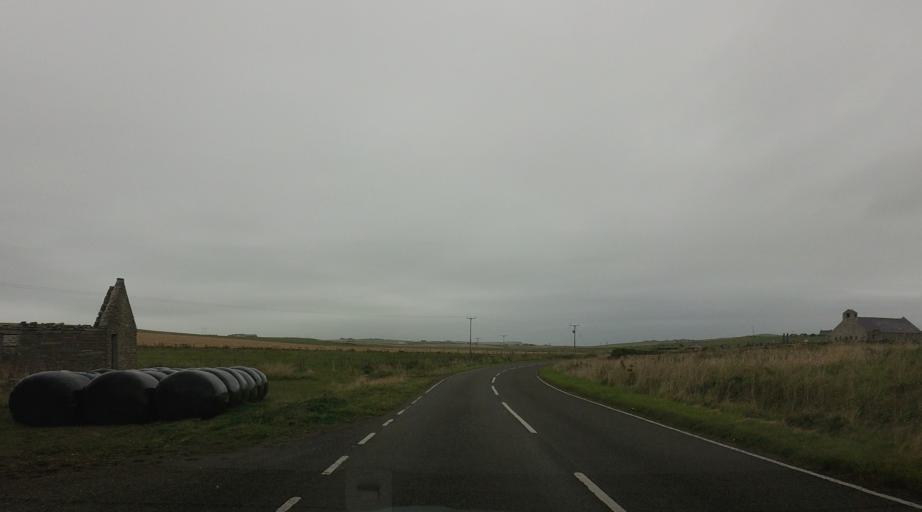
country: GB
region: Scotland
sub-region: Orkney Islands
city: Orkney
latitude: 58.7418
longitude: -2.9715
